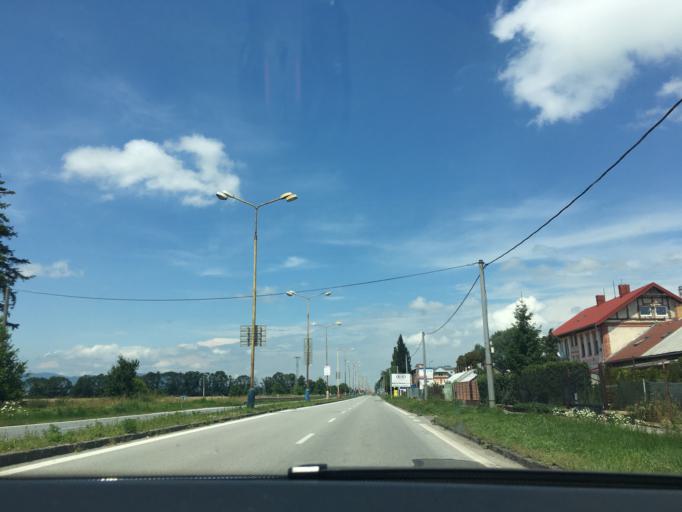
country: SK
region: Kosicky
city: Trebisov
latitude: 48.6400
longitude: 21.7162
